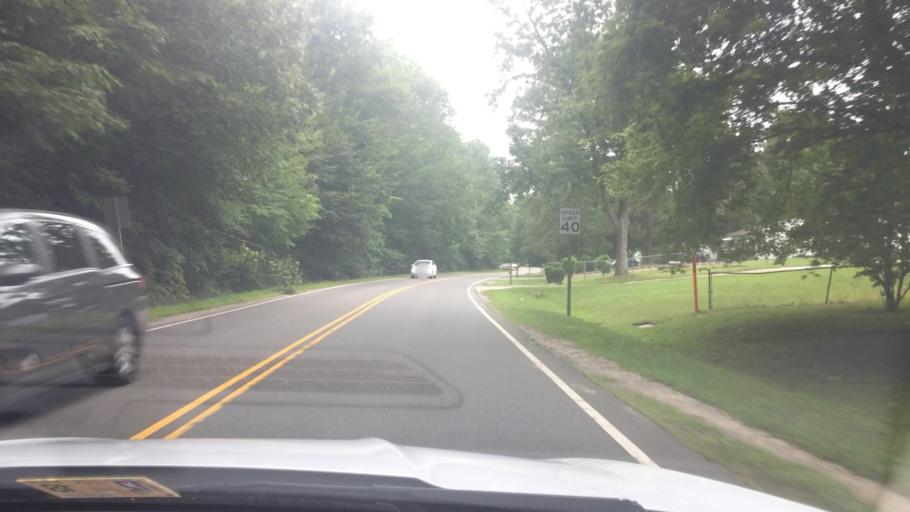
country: US
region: Virginia
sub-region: York County
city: Yorktown
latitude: 37.2282
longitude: -76.5252
